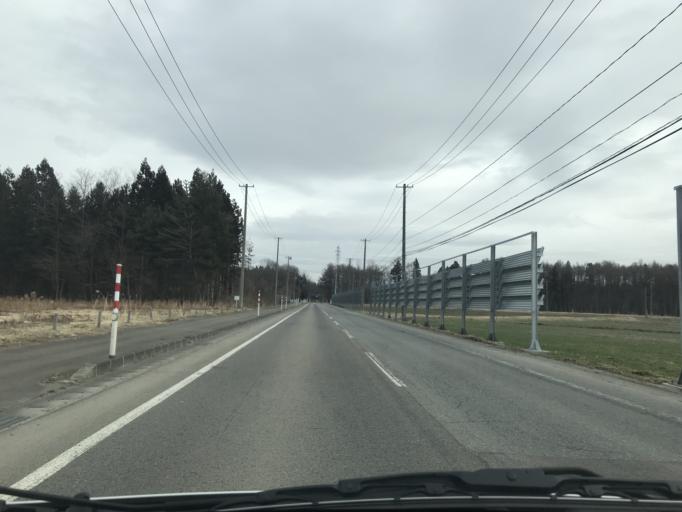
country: JP
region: Iwate
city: Kitakami
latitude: 39.3227
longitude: 141.0075
